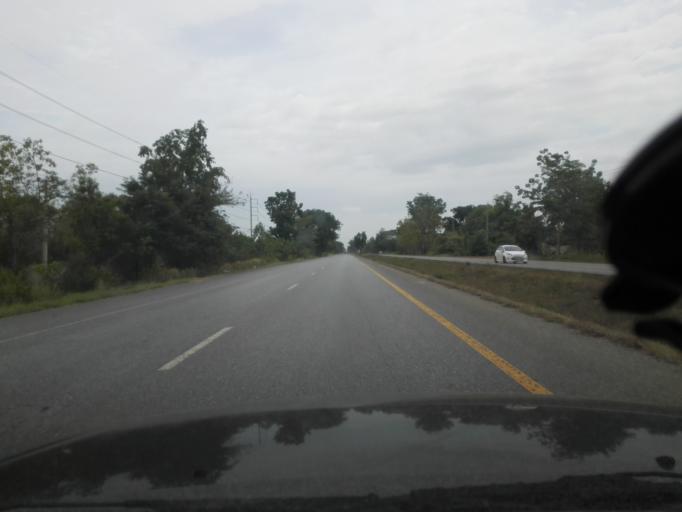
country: TH
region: Kamphaeng Phet
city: Khlong Khlung
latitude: 16.1137
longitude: 99.7193
